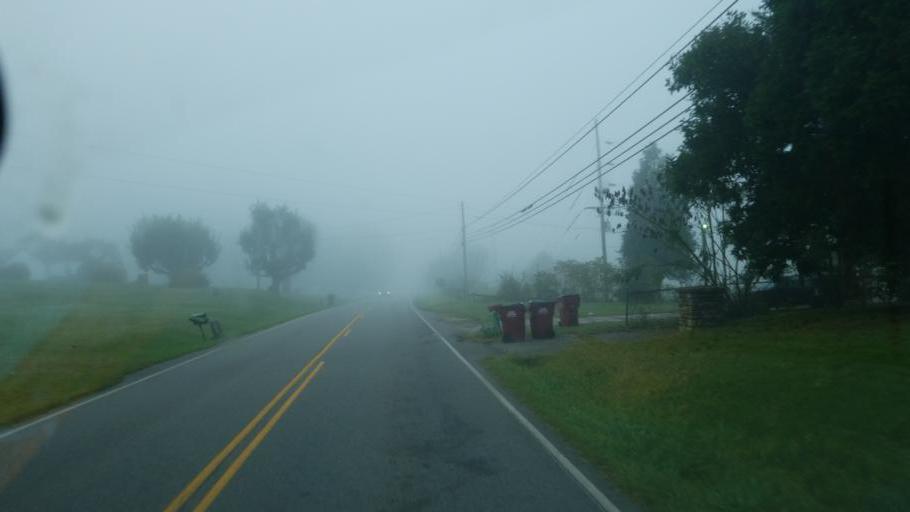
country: US
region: Ohio
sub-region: Scioto County
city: Portsmouth
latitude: 38.7142
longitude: -83.0236
